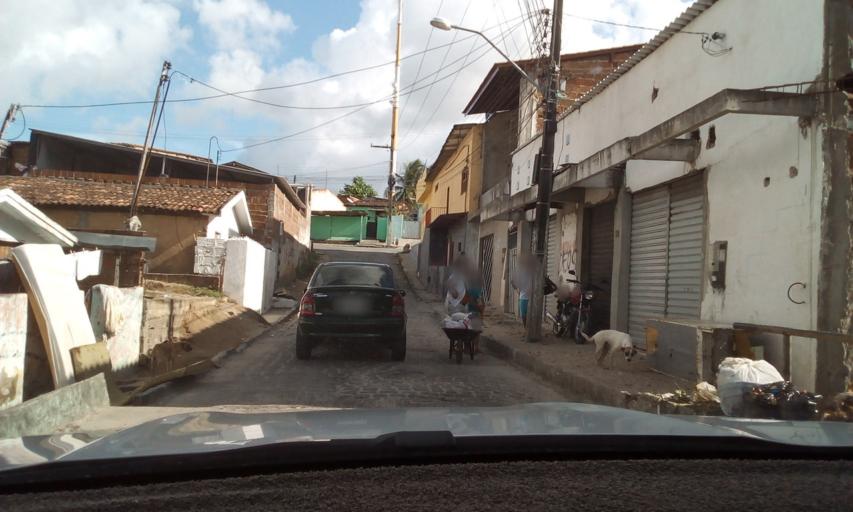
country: BR
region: Paraiba
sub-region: Bayeux
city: Bayeux
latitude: -7.1321
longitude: -34.9211
